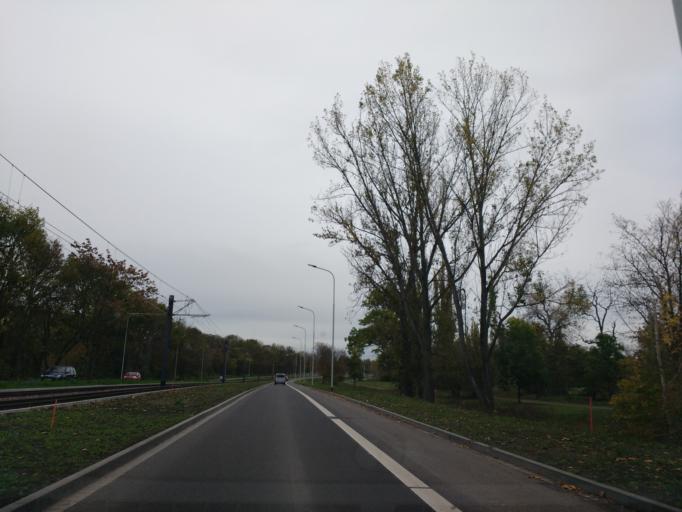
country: DE
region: Saxony-Anhalt
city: Halle Neustadt
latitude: 51.4933
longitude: 11.9422
